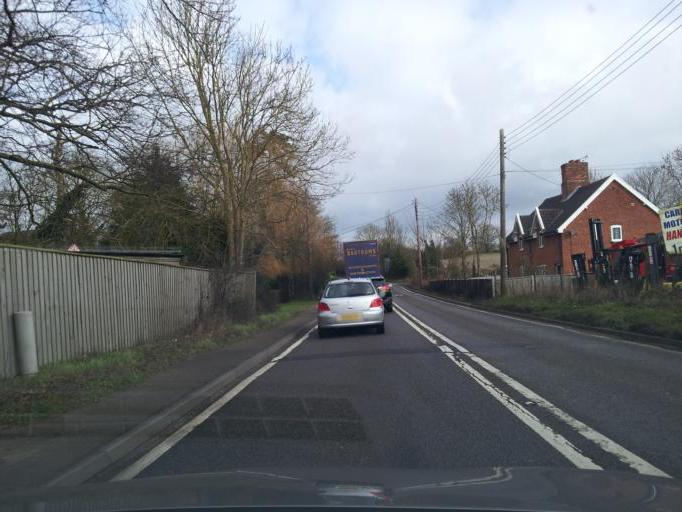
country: GB
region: England
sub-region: Suffolk
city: Needham Market
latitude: 52.1790
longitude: 1.0934
